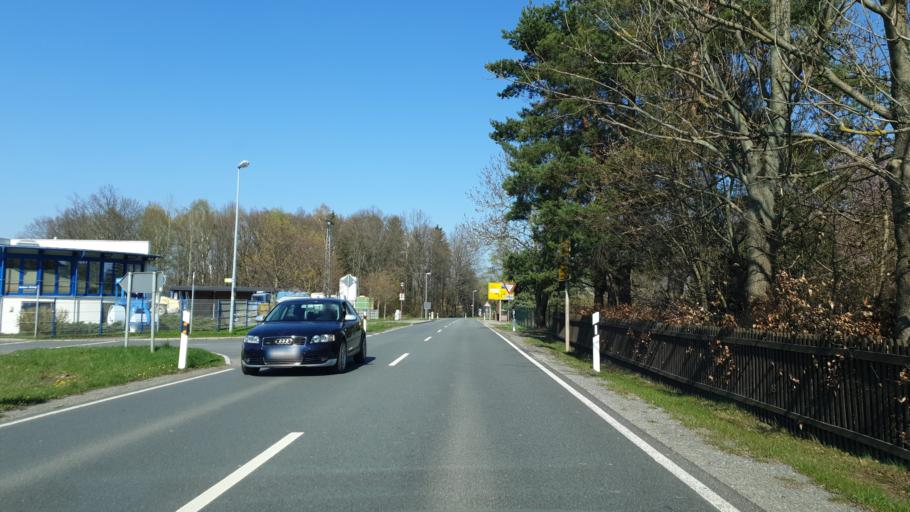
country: DE
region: Saxony
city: Oelsnitz
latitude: 50.7168
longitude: 12.7192
